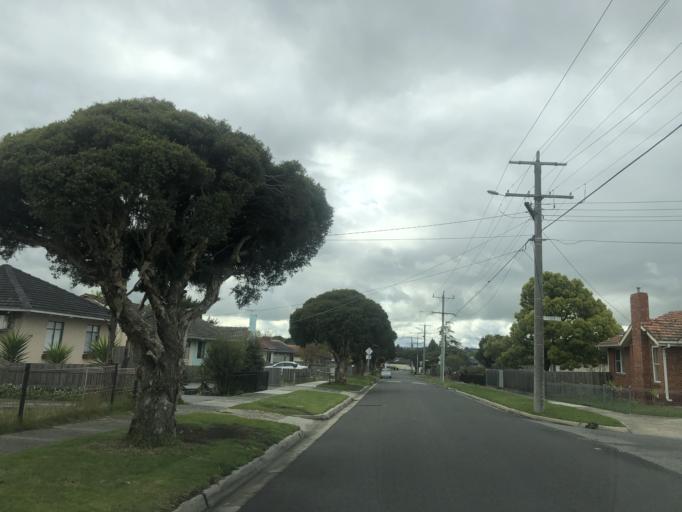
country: AU
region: Victoria
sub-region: Greater Dandenong
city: Dandenong North
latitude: -37.9648
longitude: 145.2145
